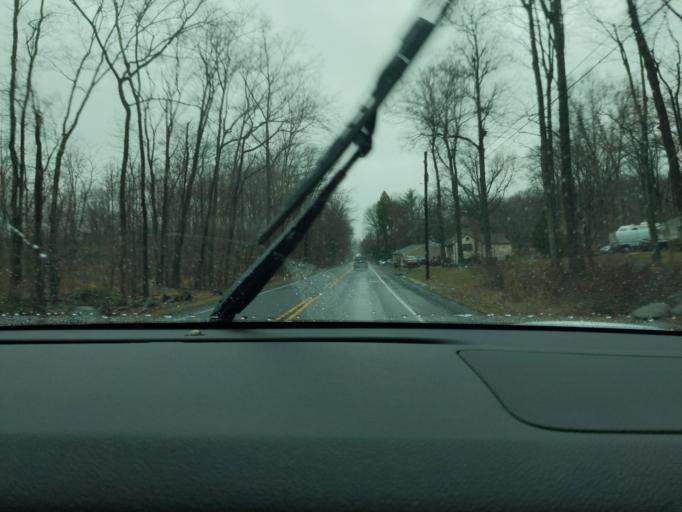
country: US
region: Pennsylvania
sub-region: Bucks County
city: Richlandtown
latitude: 40.4281
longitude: -75.2889
